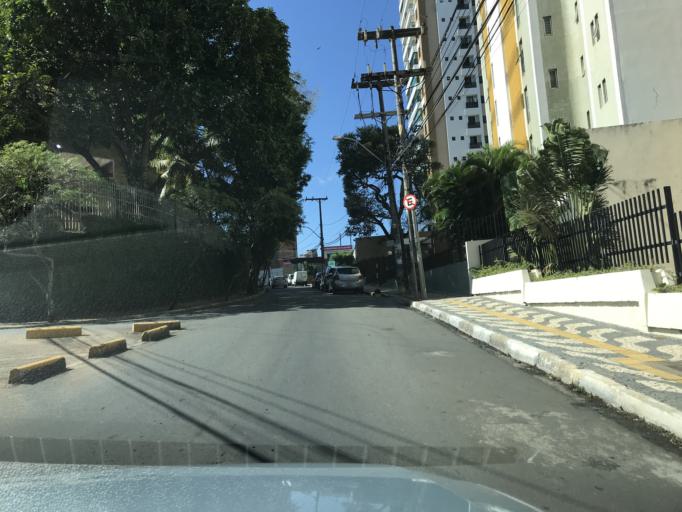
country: BR
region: Bahia
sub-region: Salvador
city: Salvador
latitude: -13.0051
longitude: -38.5161
